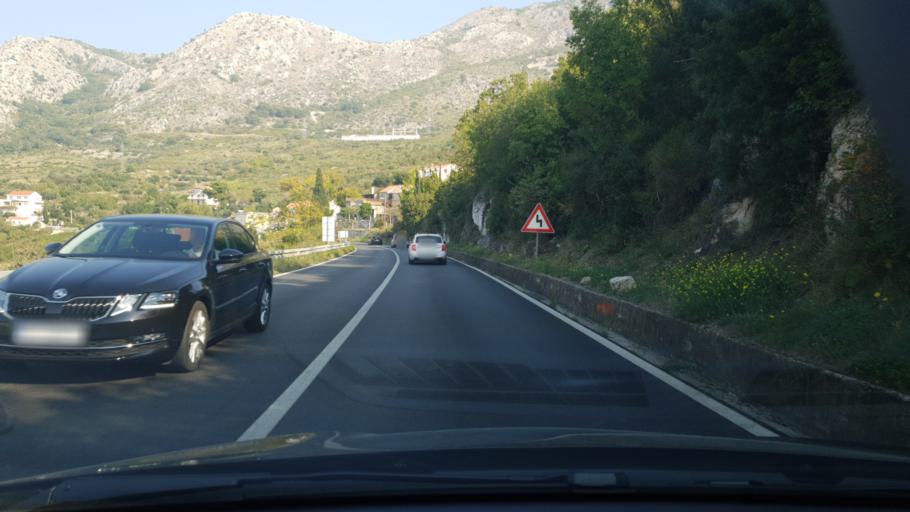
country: HR
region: Dubrovacko-Neretvanska
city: Cavtat
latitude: 42.6038
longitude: 18.2324
